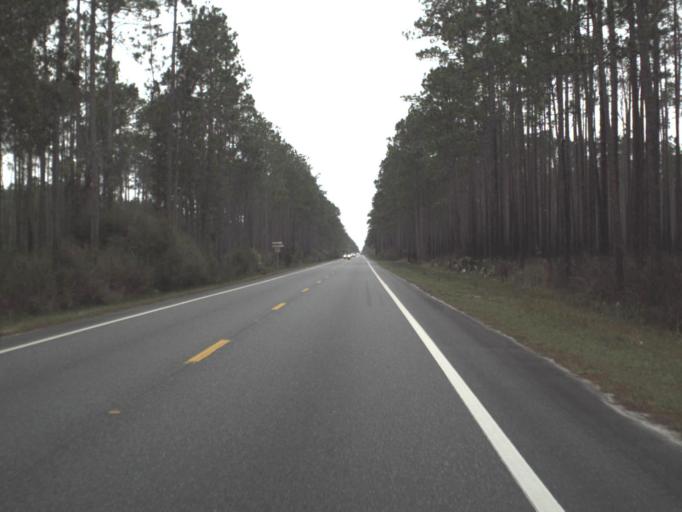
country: US
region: Florida
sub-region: Franklin County
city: Apalachicola
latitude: 29.9599
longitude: -84.9761
